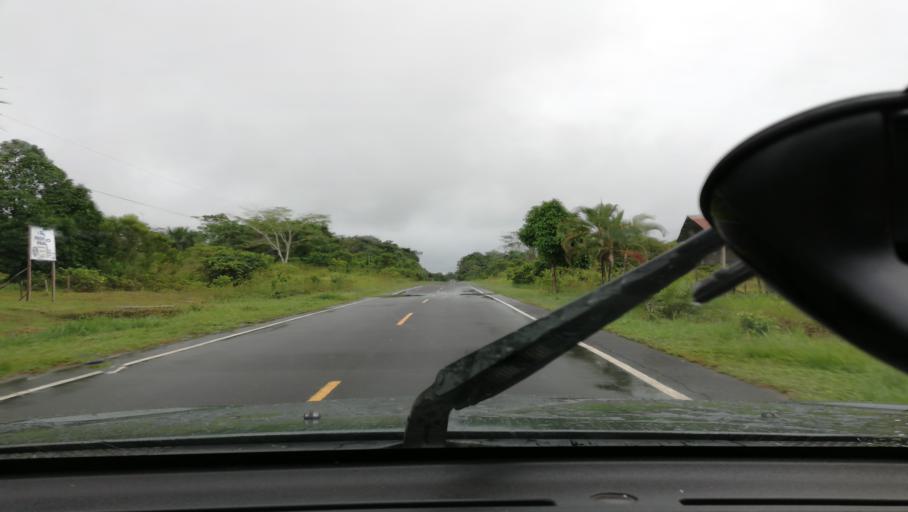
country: PE
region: Loreto
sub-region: Provincia de Maynas
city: San Juan
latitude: -4.1994
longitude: -73.4784
